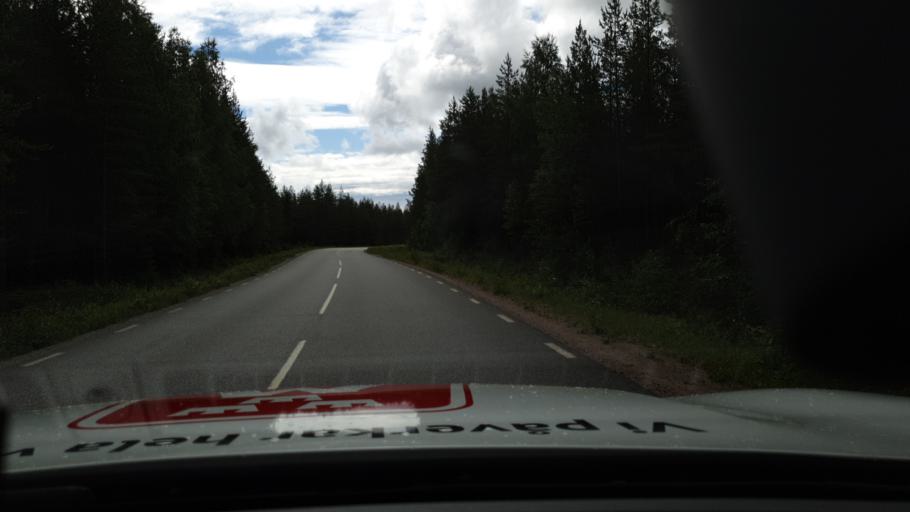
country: SE
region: Norrbotten
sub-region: Lulea Kommun
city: Sodra Sunderbyn
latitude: 65.4917
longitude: 21.8887
